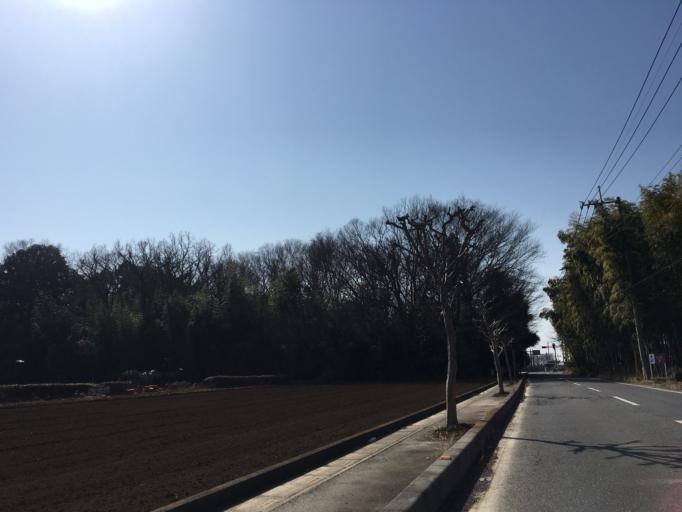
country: JP
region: Saitama
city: Oi
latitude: 35.8285
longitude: 139.5070
